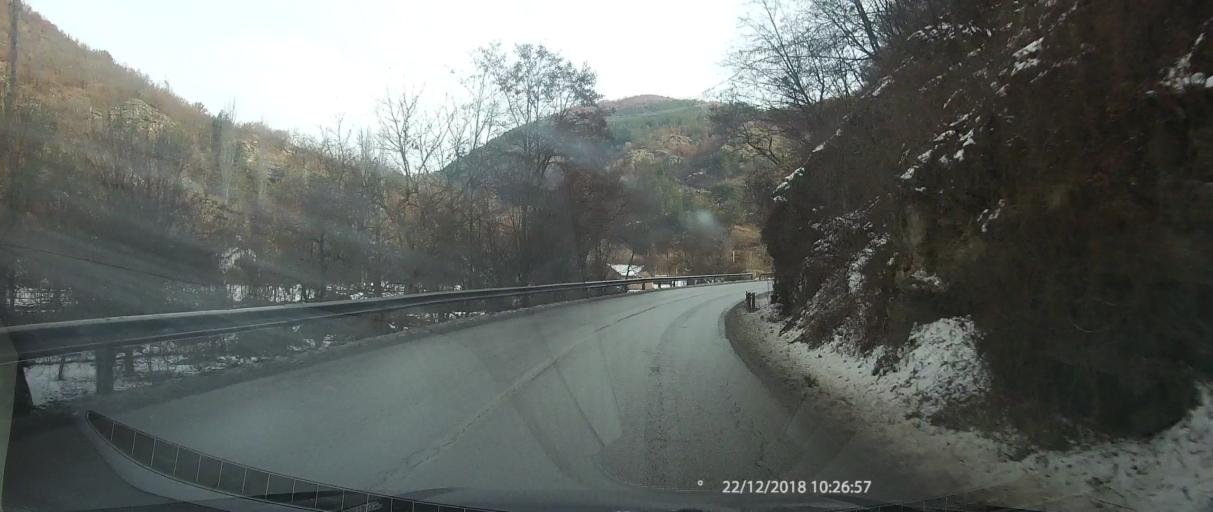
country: MK
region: Kriva Palanka
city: Kriva Palanka
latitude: 42.2298
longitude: 22.3615
